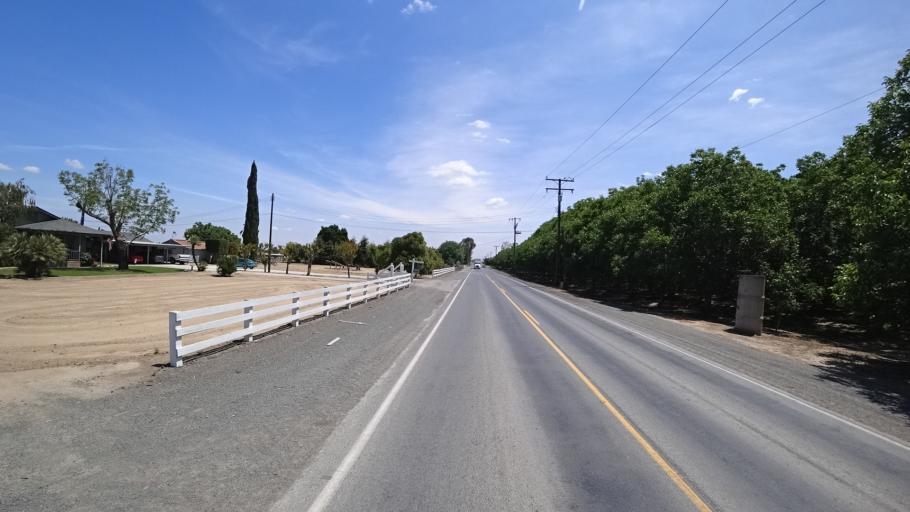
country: US
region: California
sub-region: Kings County
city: Home Garden
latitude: 36.2983
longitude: -119.6716
